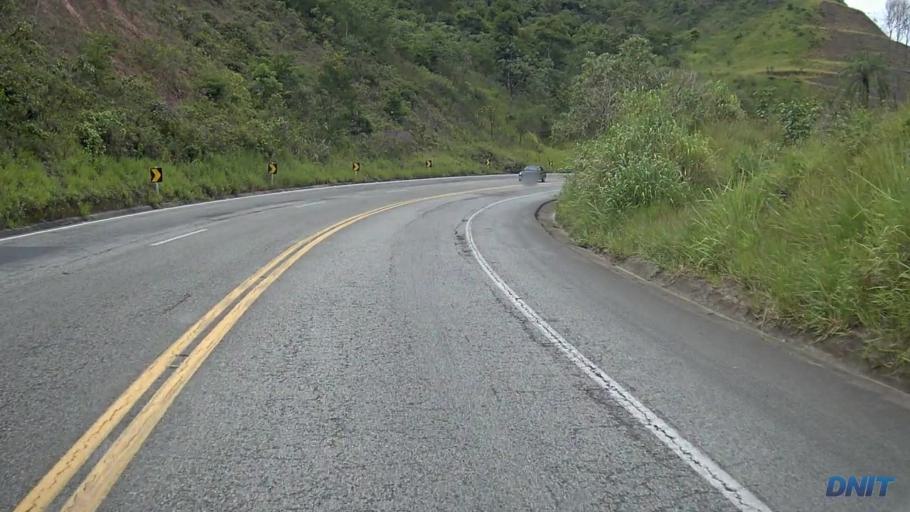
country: BR
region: Minas Gerais
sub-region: Nova Era
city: Nova Era
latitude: -19.6317
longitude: -42.8971
